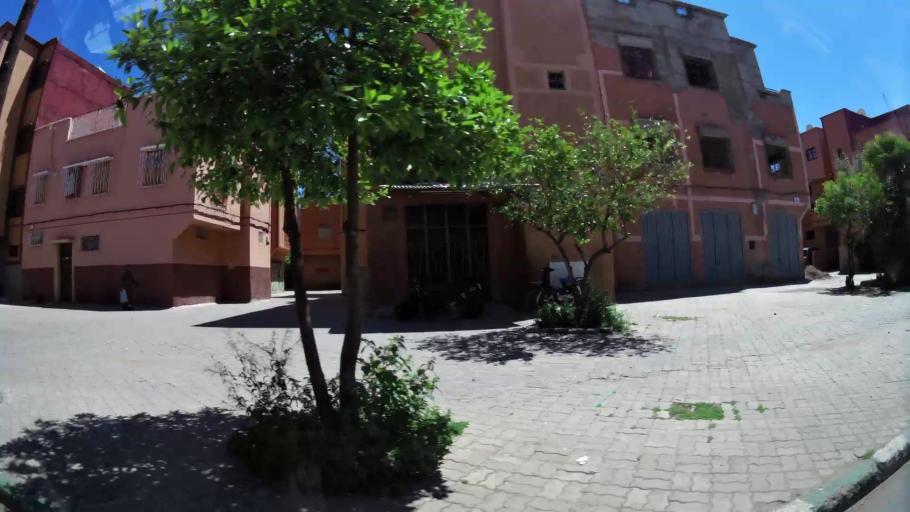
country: MA
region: Marrakech-Tensift-Al Haouz
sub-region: Marrakech
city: Marrakesh
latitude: 31.6323
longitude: -8.0502
